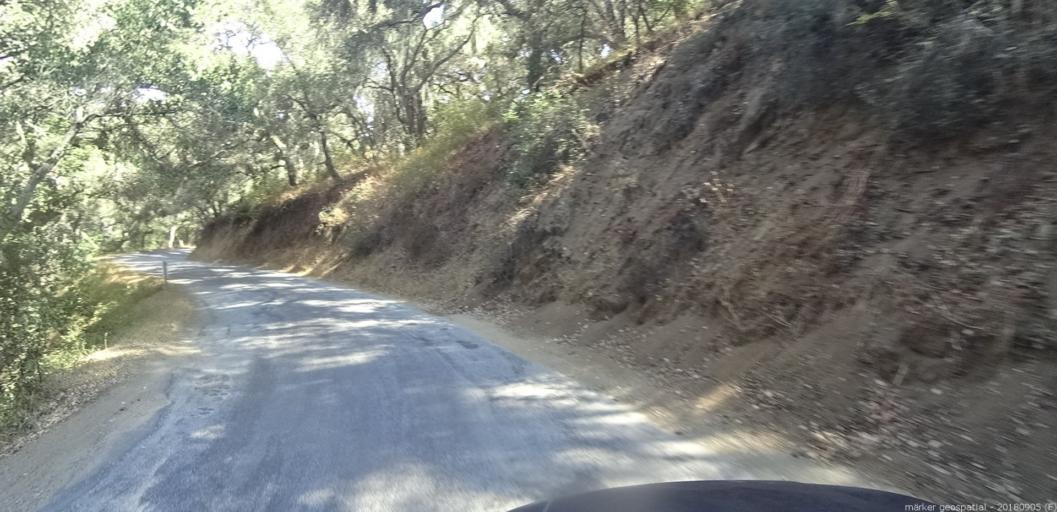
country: US
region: California
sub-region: Monterey County
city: Carmel Valley Village
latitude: 36.4436
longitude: -121.6865
